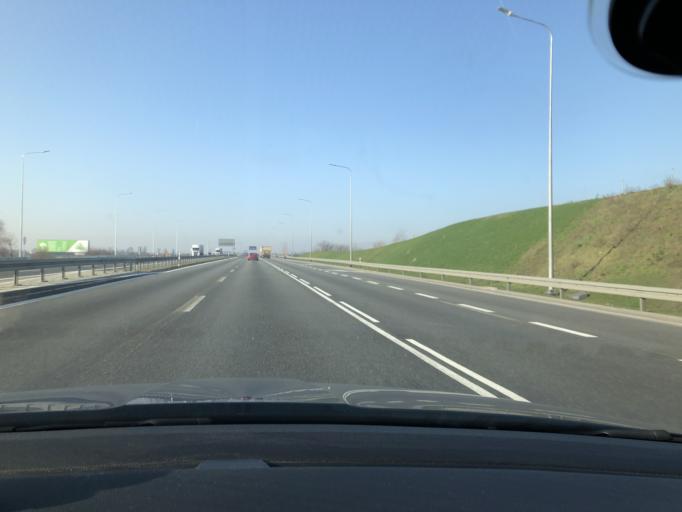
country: PL
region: Greater Poland Voivodeship
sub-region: Powiat poznanski
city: Daszewice
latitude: 52.3475
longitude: 16.9807
